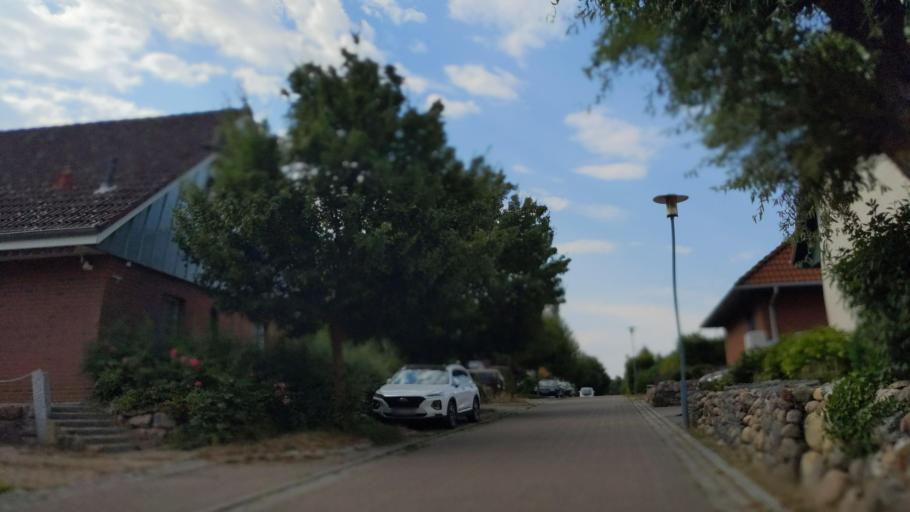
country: DE
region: Schleswig-Holstein
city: Gross Gronau
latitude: 53.8413
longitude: 10.7694
